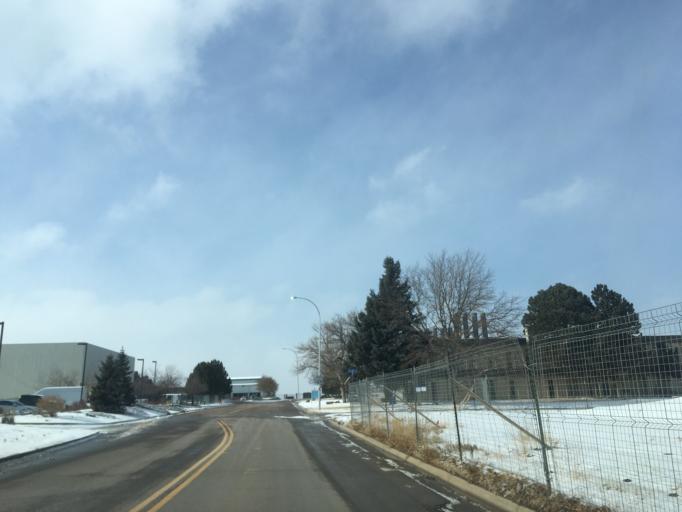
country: US
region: Colorado
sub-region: Broomfield County
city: Broomfield
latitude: 39.9117
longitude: -105.1061
